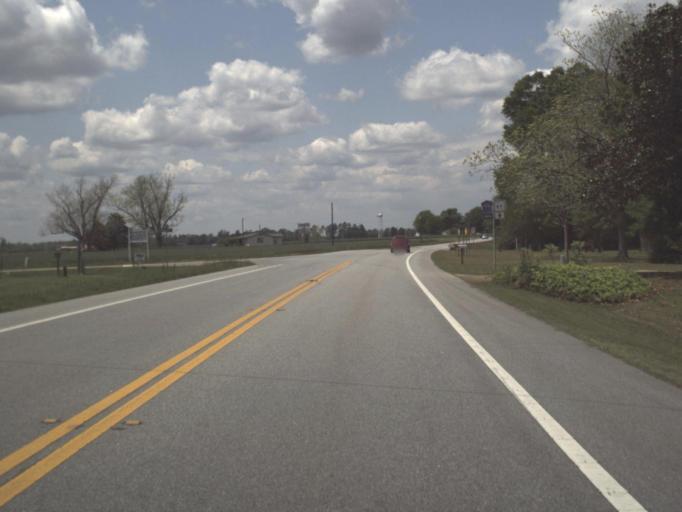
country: US
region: Alabama
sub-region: Escambia County
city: Atmore
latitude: 30.8889
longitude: -87.4624
